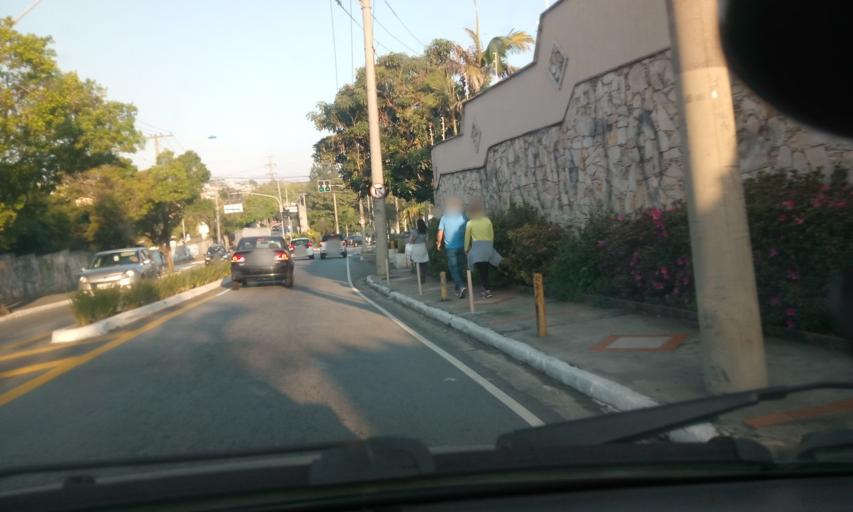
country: BR
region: Sao Paulo
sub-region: Sao Caetano Do Sul
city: Sao Caetano do Sul
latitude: -23.6376
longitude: -46.5756
